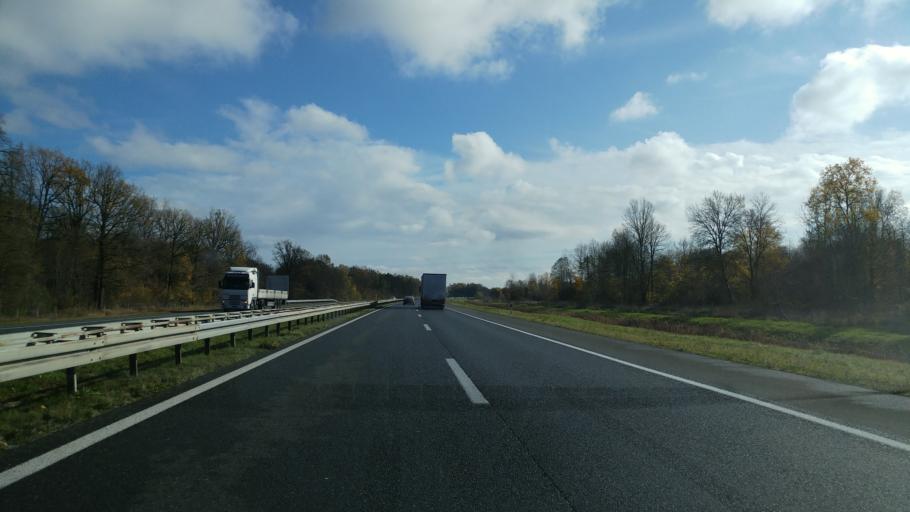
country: HR
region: Zagrebacka
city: Lupoglav
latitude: 45.7464
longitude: 16.3170
